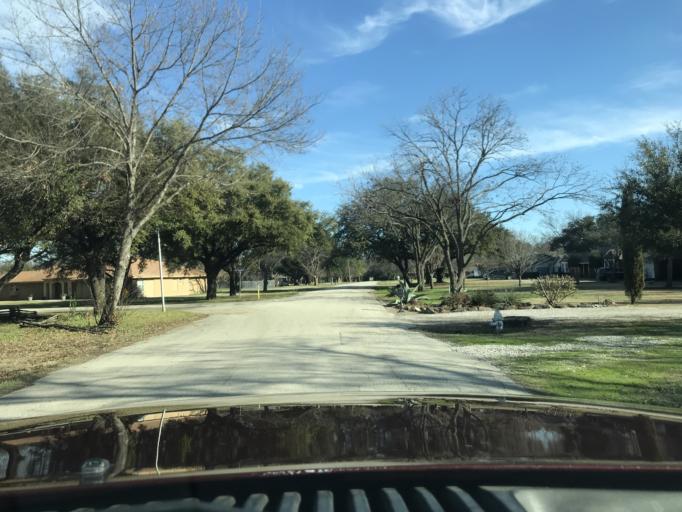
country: US
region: Texas
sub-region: Tarrant County
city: Edgecliff Village
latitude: 32.6586
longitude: -97.3456
